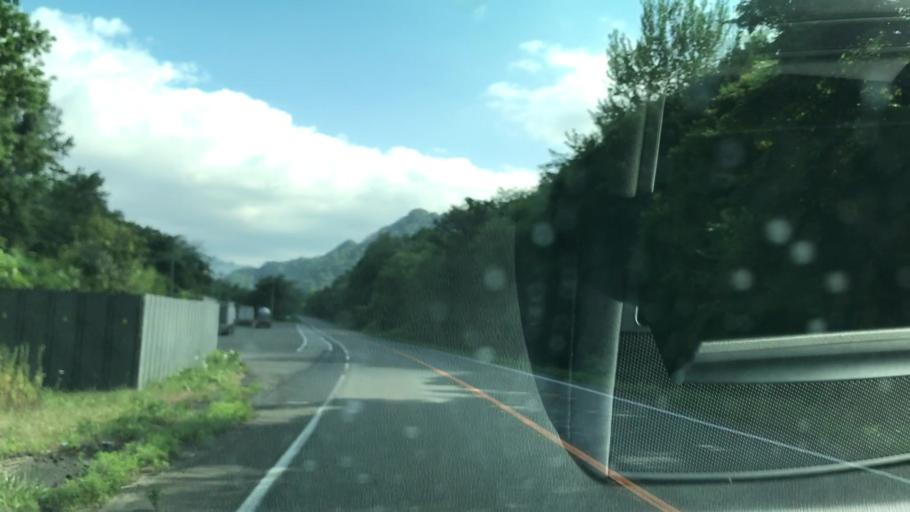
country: JP
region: Hokkaido
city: Shizunai-furukawacho
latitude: 42.8389
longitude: 142.4158
